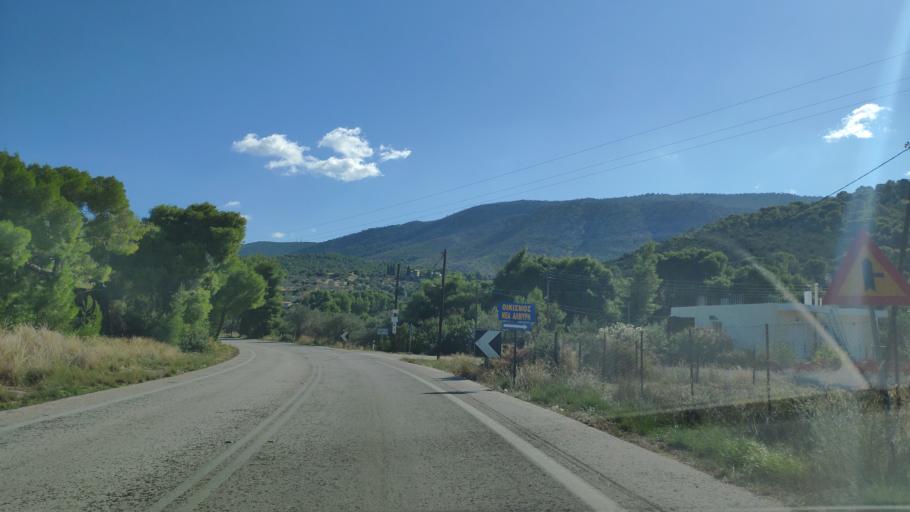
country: GR
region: Peloponnese
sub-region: Nomos Korinthias
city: Loutra Oraias Elenis
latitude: 37.8376
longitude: 23.0041
